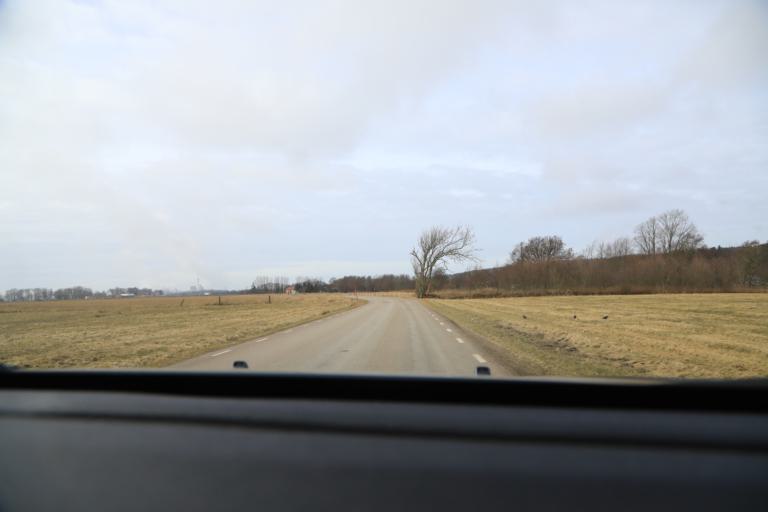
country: SE
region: Halland
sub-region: Varbergs Kommun
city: Veddige
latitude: 57.2287
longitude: 12.2403
